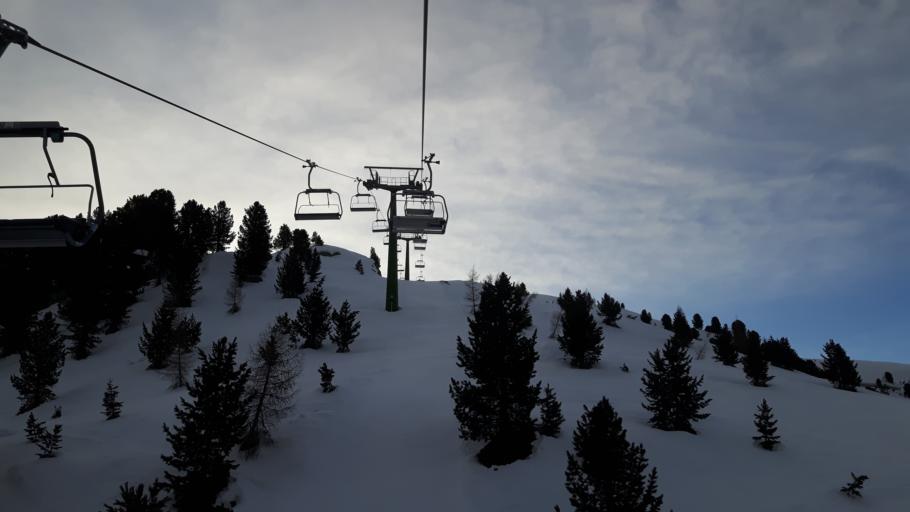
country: IT
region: Trentino-Alto Adige
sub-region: Provincia di Trento
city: Panchia
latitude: 46.3366
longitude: 11.5453
